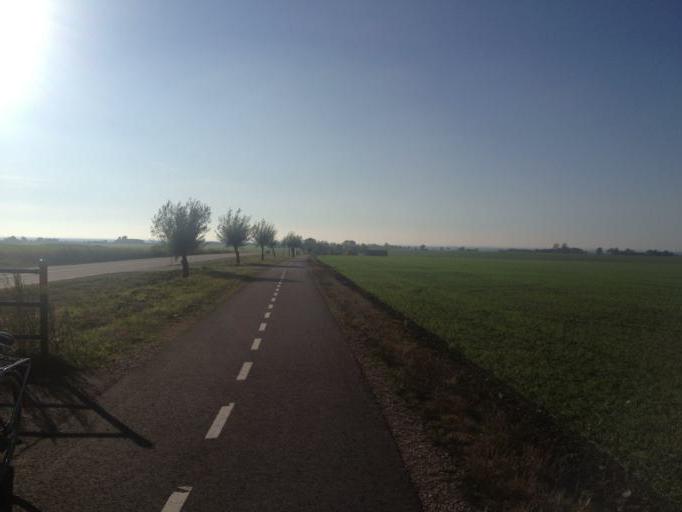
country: SE
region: Skane
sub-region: Kavlinge Kommun
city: Hofterup
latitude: 55.7647
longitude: 12.9460
